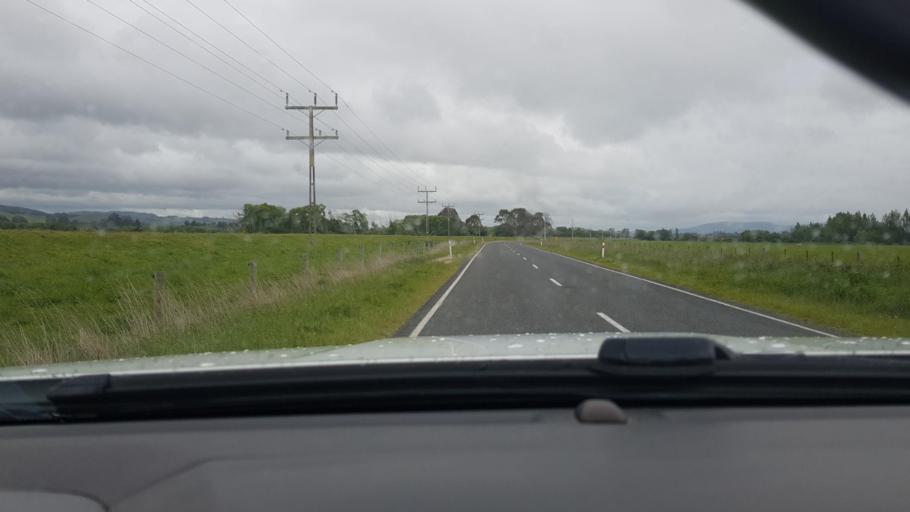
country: NZ
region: Southland
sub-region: Southland District
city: Winton
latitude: -45.8375
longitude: 168.3701
